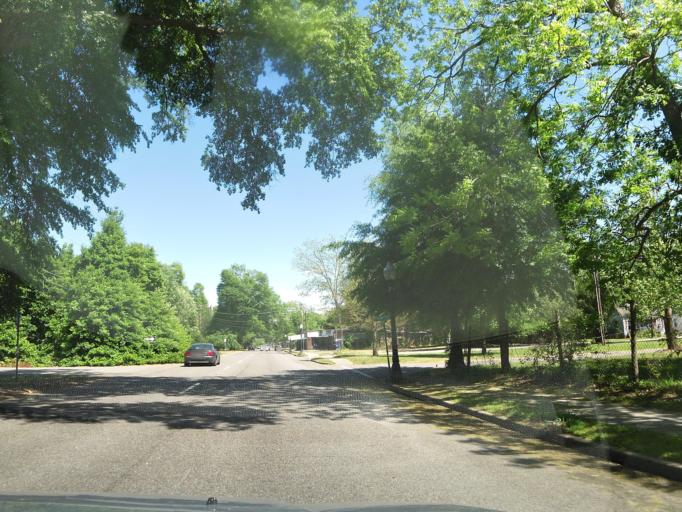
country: US
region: South Carolina
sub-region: Aiken County
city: Aiken
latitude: 33.5584
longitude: -81.7129
